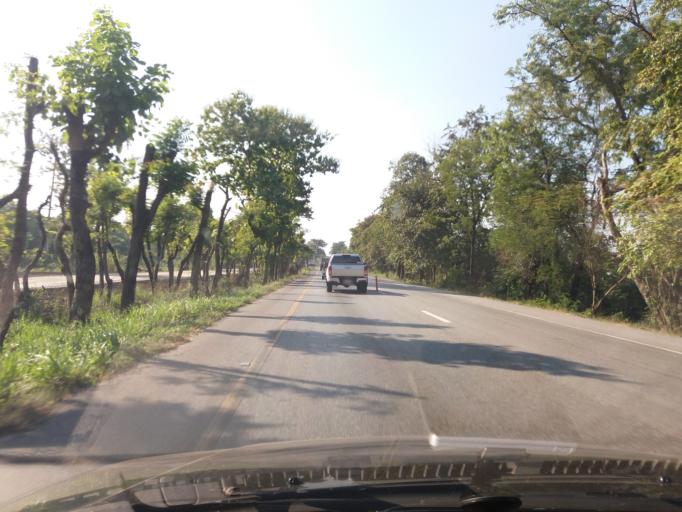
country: TH
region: Nakhon Sawan
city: Nakhon Sawan
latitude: 15.7387
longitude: 100.0185
